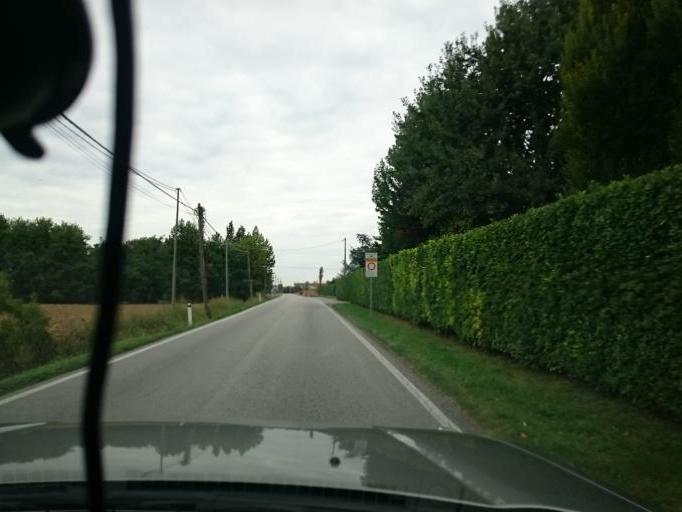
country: IT
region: Veneto
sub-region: Provincia di Padova
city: Mestrino
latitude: 45.4301
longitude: 11.7380
